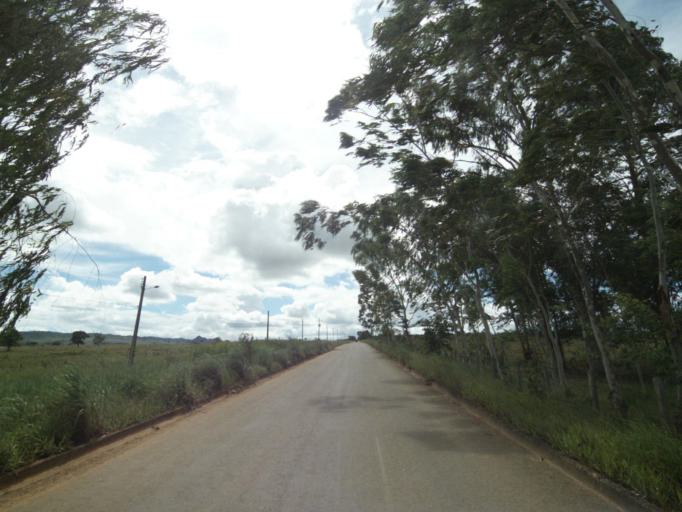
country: BR
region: Goias
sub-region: Pirenopolis
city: Pirenopolis
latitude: -15.7877
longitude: -48.7791
